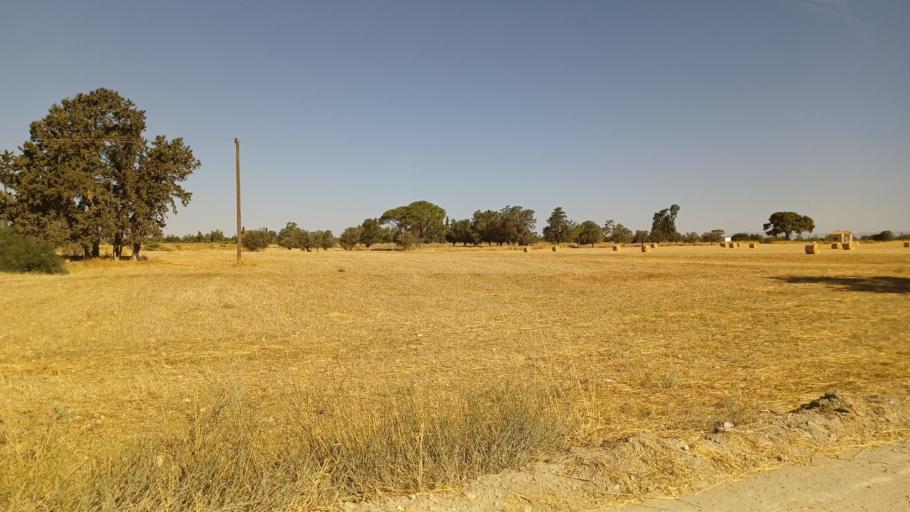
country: CY
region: Larnaka
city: Pergamos
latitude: 35.0405
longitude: 33.7027
